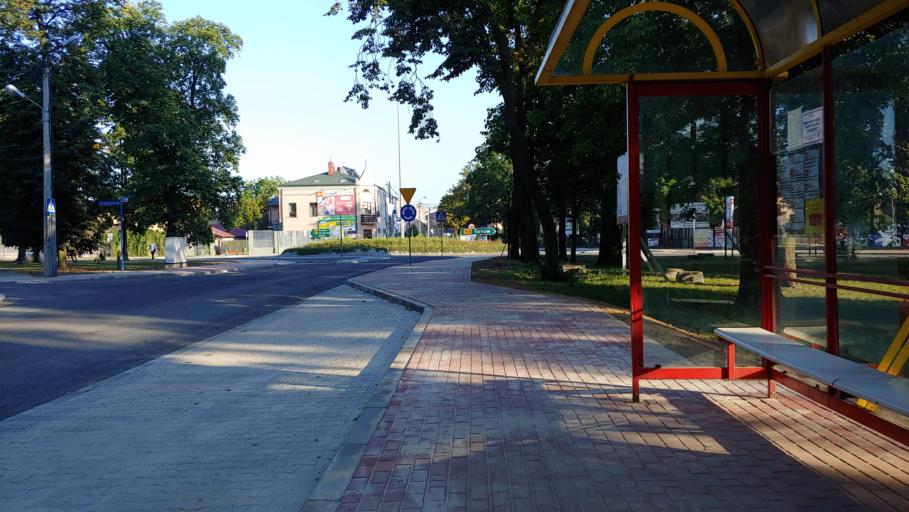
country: PL
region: Subcarpathian Voivodeship
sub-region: Powiat mielecki
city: Mielec
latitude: 50.2890
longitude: 21.4156
